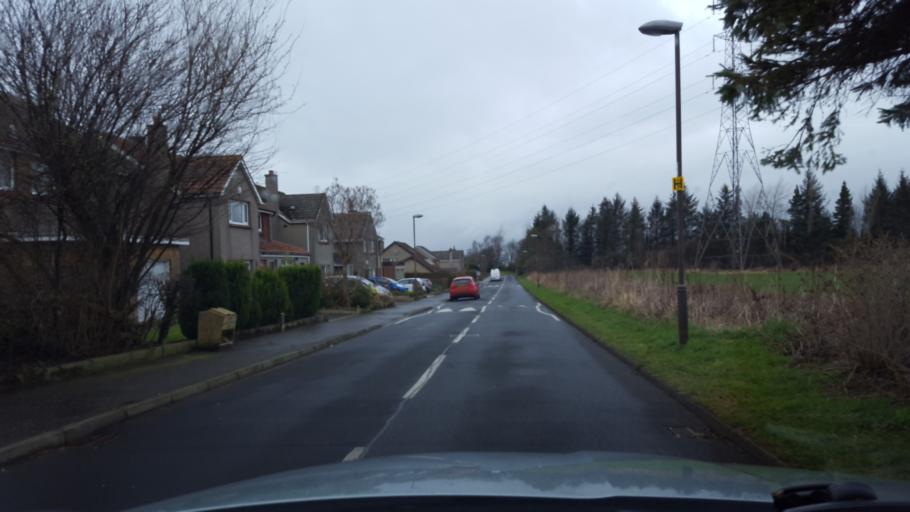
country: GB
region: Scotland
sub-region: Edinburgh
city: Currie
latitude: 55.9022
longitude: -3.2957
